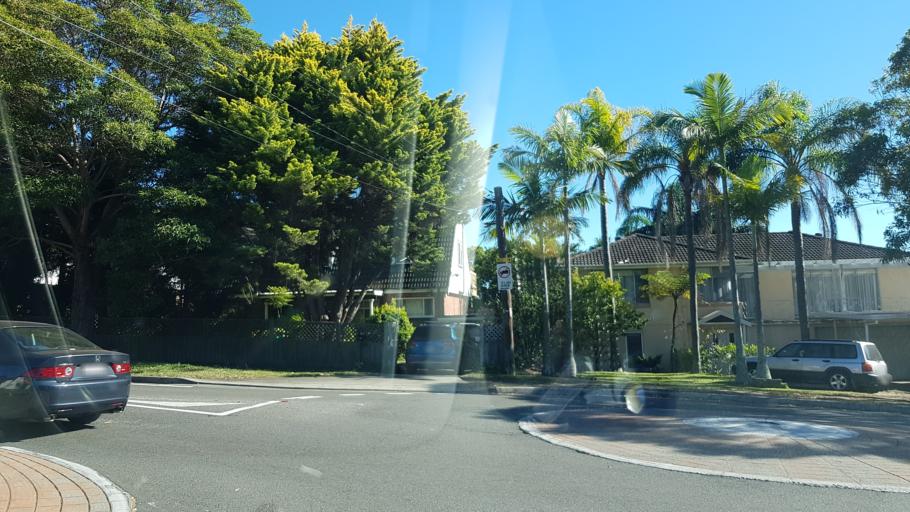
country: AU
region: New South Wales
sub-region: Pittwater
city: Warriewood
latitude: -33.6955
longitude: 151.2800
